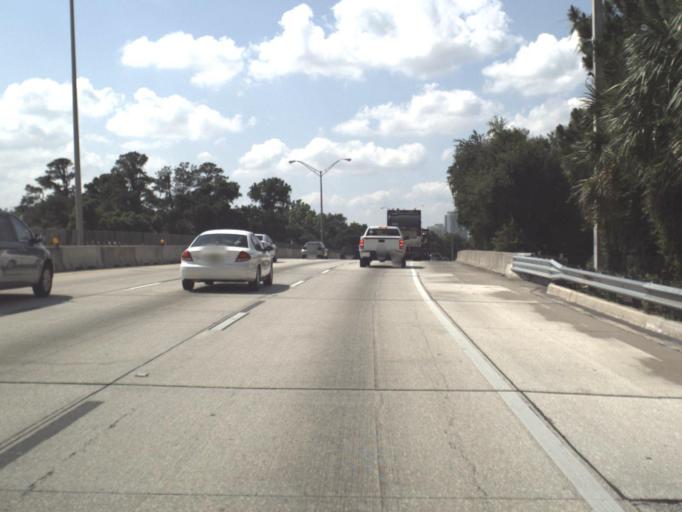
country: US
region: Florida
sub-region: Duval County
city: Jacksonville
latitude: 30.2993
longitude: -81.6389
